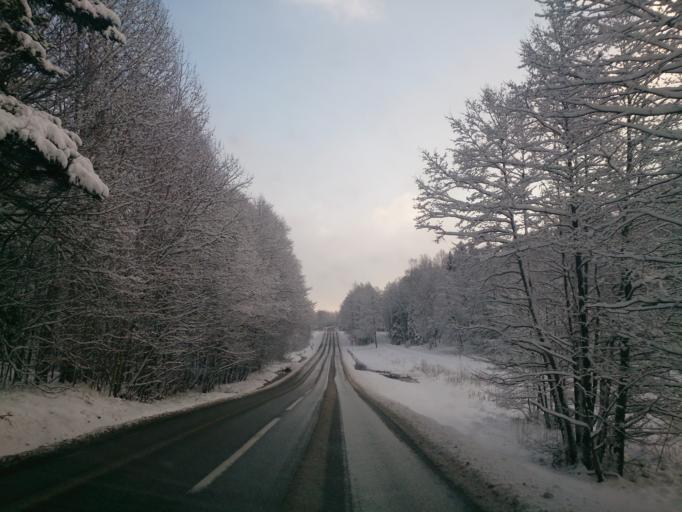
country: SE
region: Stockholm
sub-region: Varmdo Kommun
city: Hemmesta
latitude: 59.3038
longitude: 18.4957
